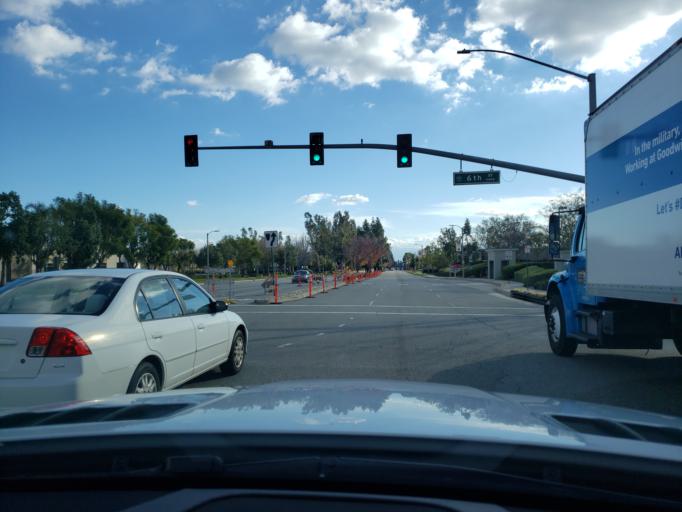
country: US
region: California
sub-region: San Bernardino County
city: Rancho Cucamonga
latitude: 34.0845
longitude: -117.5584
